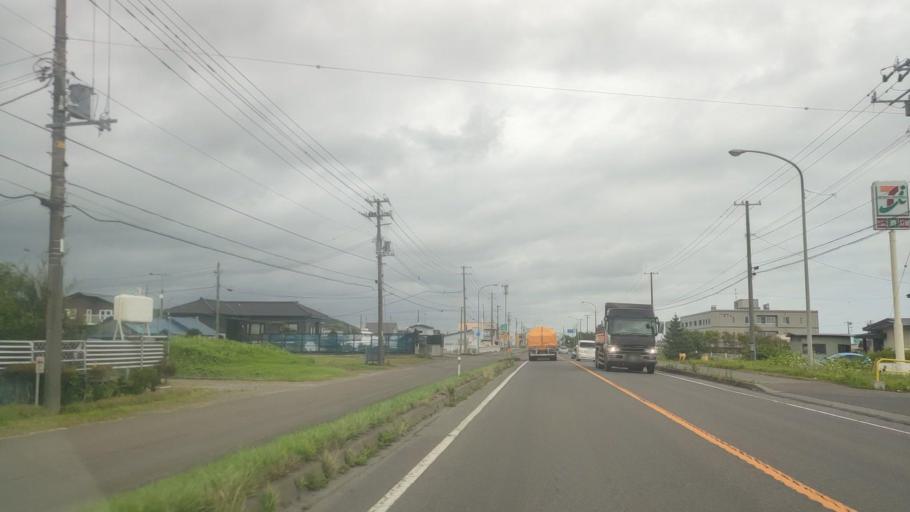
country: JP
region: Hokkaido
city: Shiraoi
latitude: 42.5152
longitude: 141.2987
